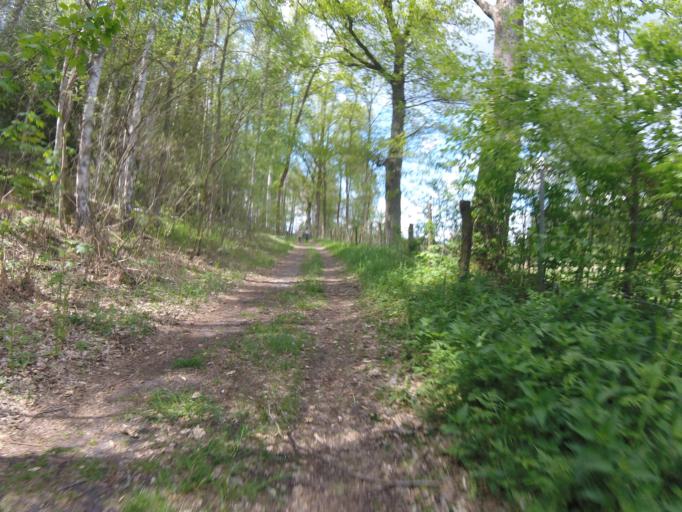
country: DE
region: Brandenburg
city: Teupitz
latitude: 52.1168
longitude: 13.6062
